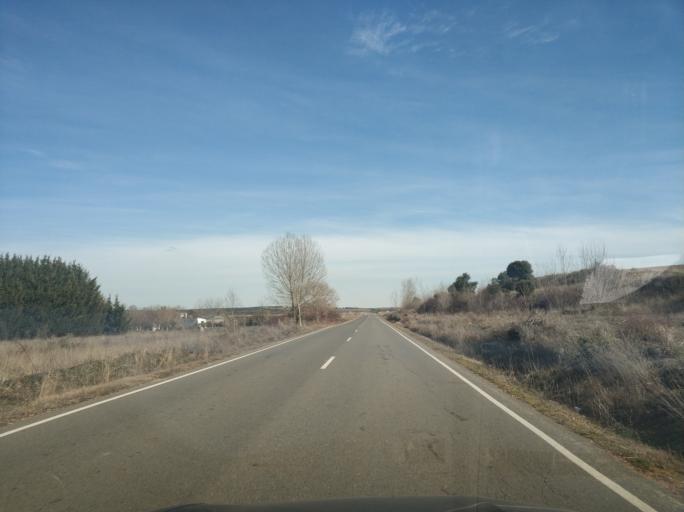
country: ES
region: Castille and Leon
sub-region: Provincia de Salamanca
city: Valverdon
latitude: 41.0378
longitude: -5.7821
